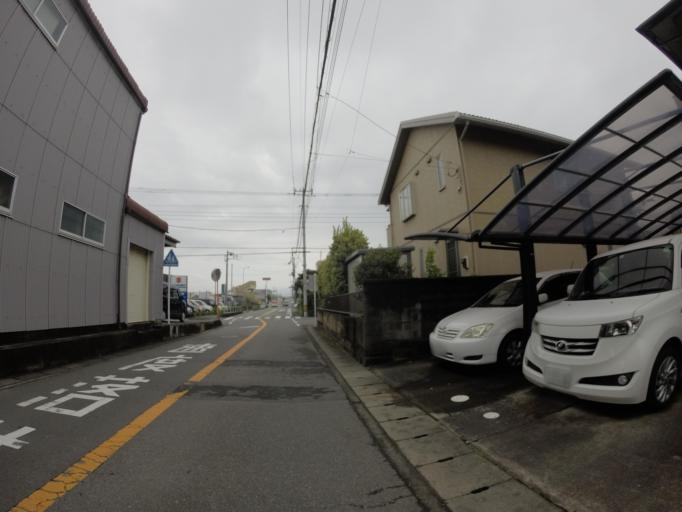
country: JP
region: Shizuoka
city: Numazu
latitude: 35.1212
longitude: 138.8533
